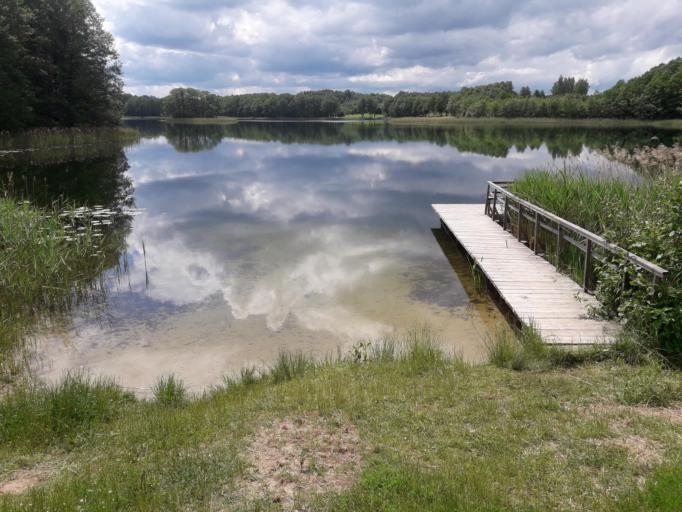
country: LT
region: Alytaus apskritis
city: Druskininkai
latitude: 54.1088
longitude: 24.0208
